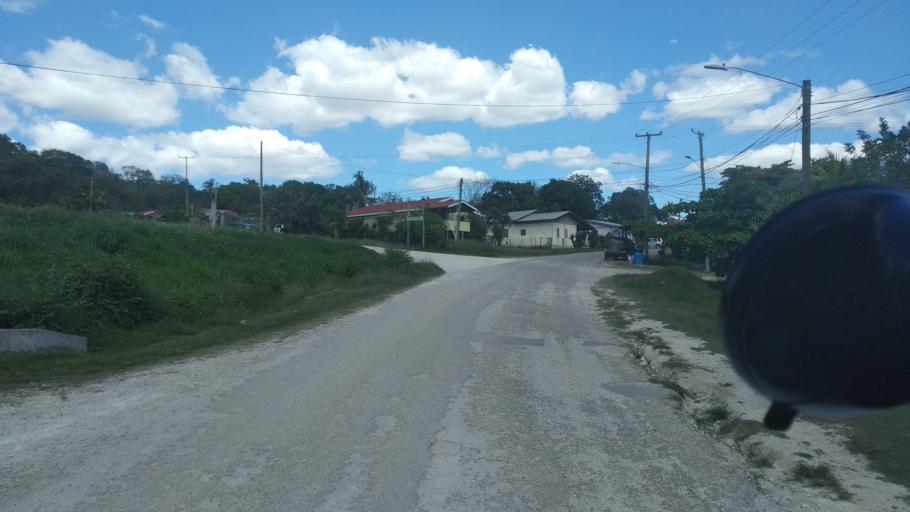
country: BZ
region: Cayo
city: Benque Viejo del Carmen
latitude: 17.0763
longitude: -89.1314
